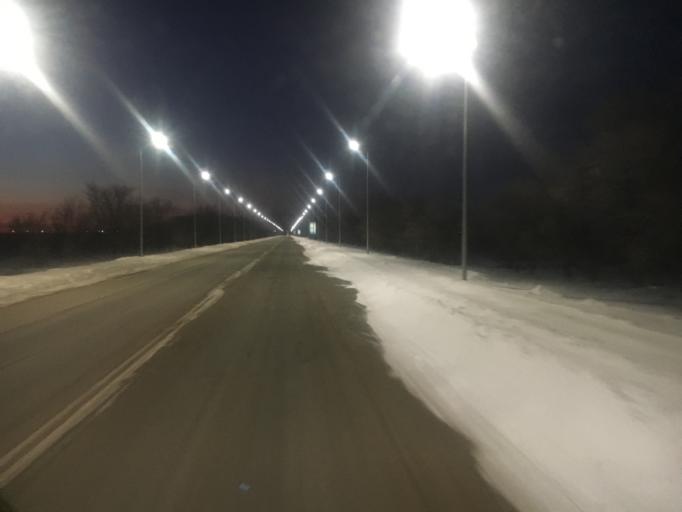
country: KZ
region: Batys Qazaqstan
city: Oral
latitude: 51.1558
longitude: 51.5358
